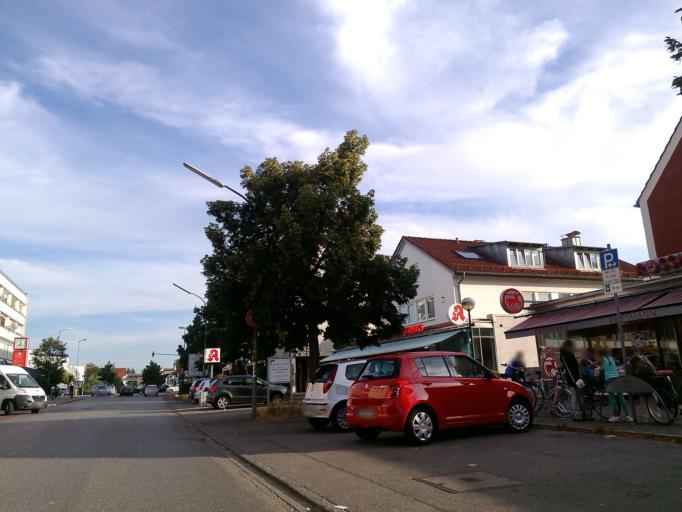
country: DE
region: Bavaria
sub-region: Upper Bavaria
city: Germering
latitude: 48.1319
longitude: 11.3643
